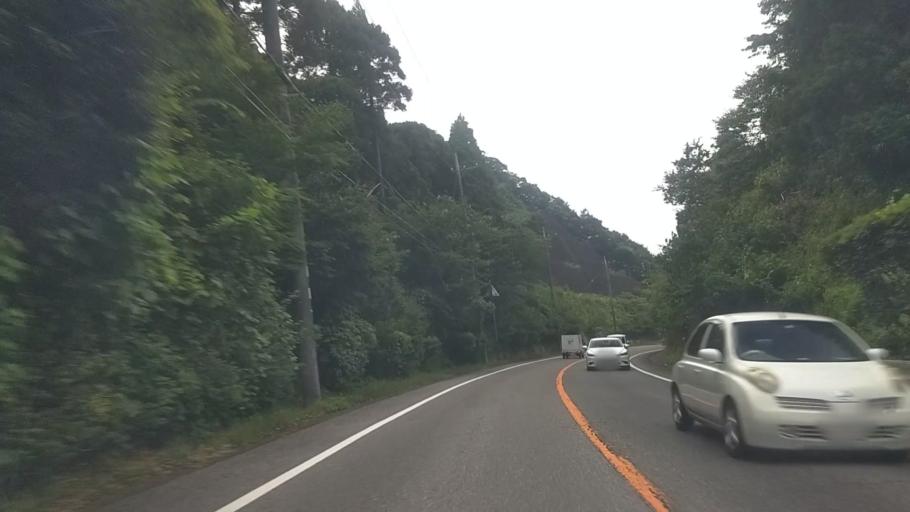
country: JP
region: Chiba
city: Kawaguchi
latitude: 35.1487
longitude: 140.0685
